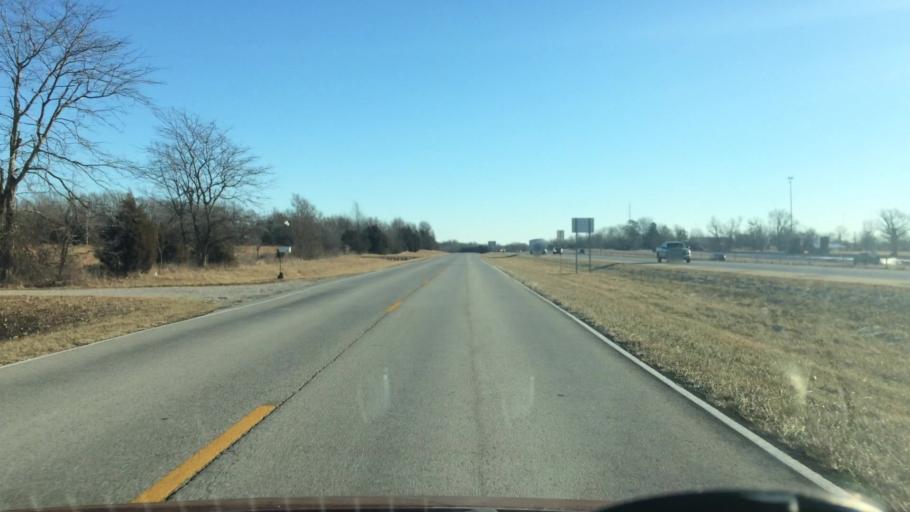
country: US
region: Missouri
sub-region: Greene County
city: Strafford
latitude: 37.2727
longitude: -93.0588
